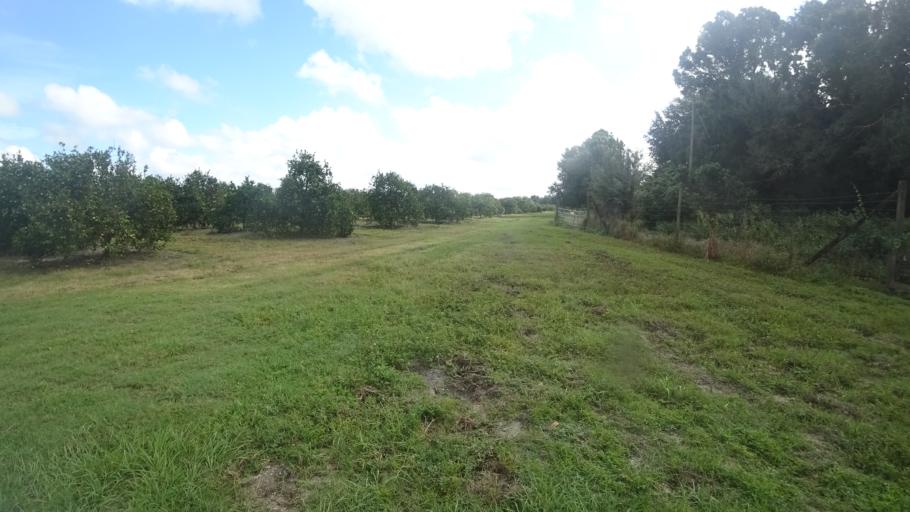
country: US
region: Florida
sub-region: Hillsborough County
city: Wimauma
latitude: 27.5337
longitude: -82.0998
